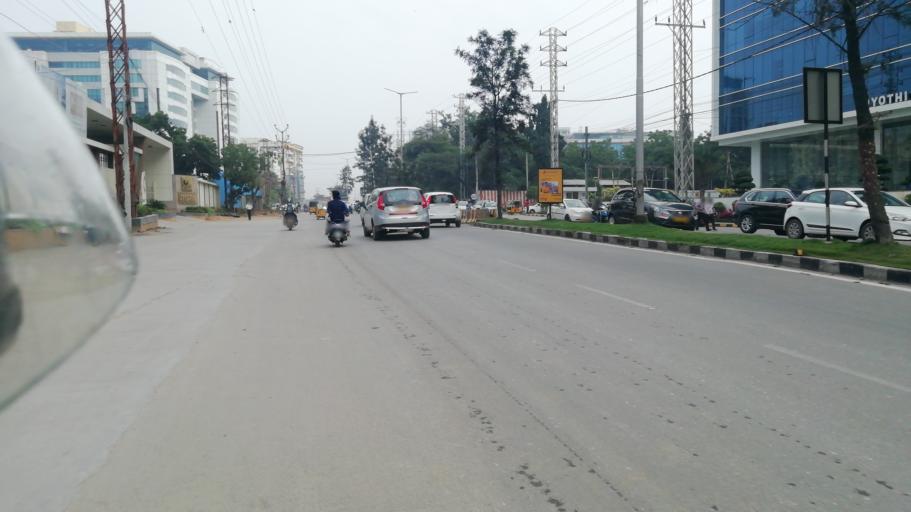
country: IN
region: Telangana
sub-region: Rangareddi
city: Kukatpalli
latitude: 17.4585
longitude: 78.3685
